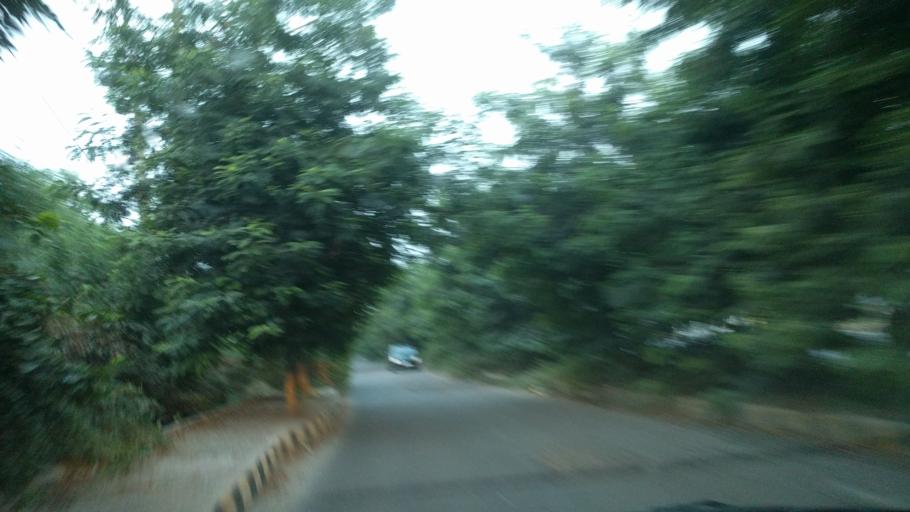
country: IN
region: Haryana
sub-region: Gurgaon
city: Gurgaon
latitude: 28.4516
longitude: 77.0653
